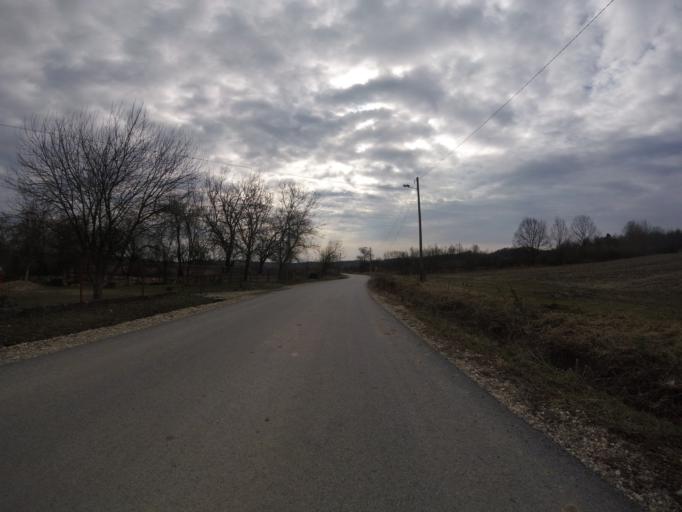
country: HR
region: Sisacko-Moslavacka
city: Glina
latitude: 45.4466
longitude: 16.0694
